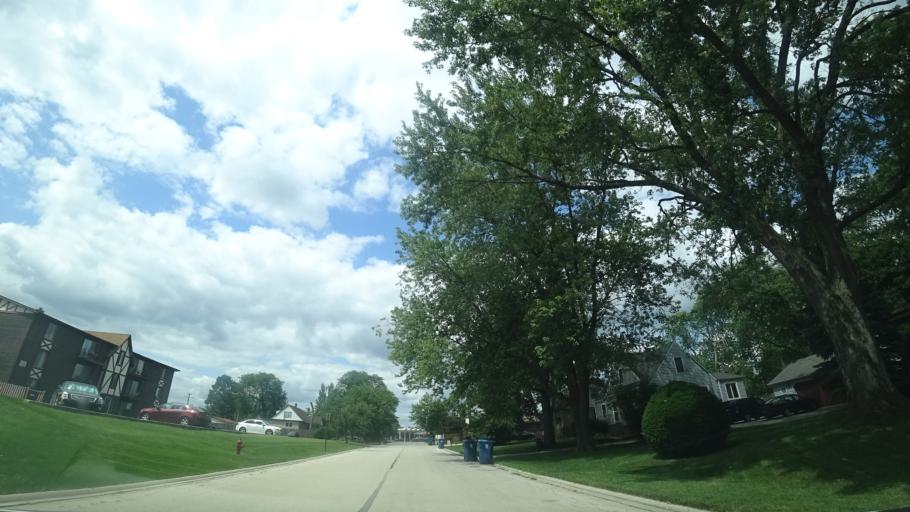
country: US
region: Illinois
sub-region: Cook County
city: Alsip
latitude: 41.6827
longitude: -87.7248
